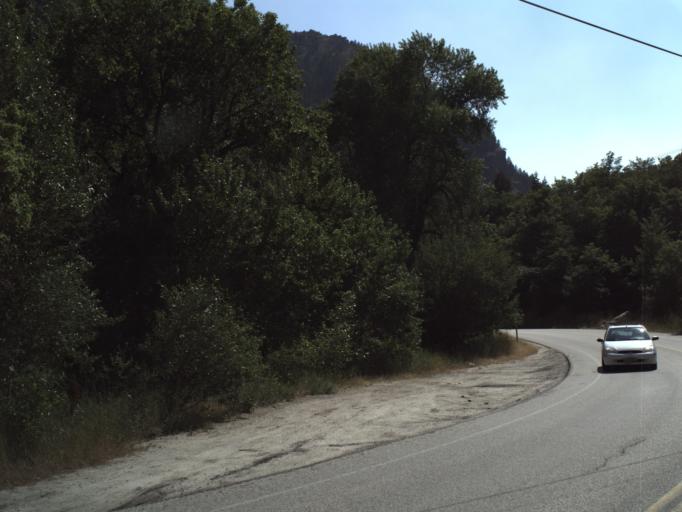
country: US
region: Utah
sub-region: Weber County
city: Liberty
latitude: 41.2546
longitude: -111.8662
